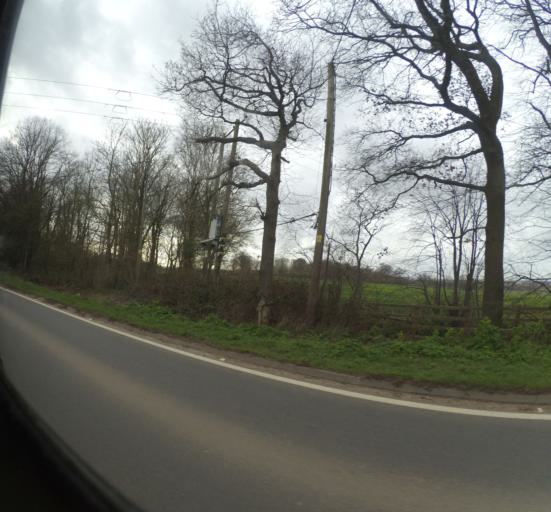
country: GB
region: England
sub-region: Warwickshire
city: Brandon
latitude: 52.4116
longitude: -1.3869
